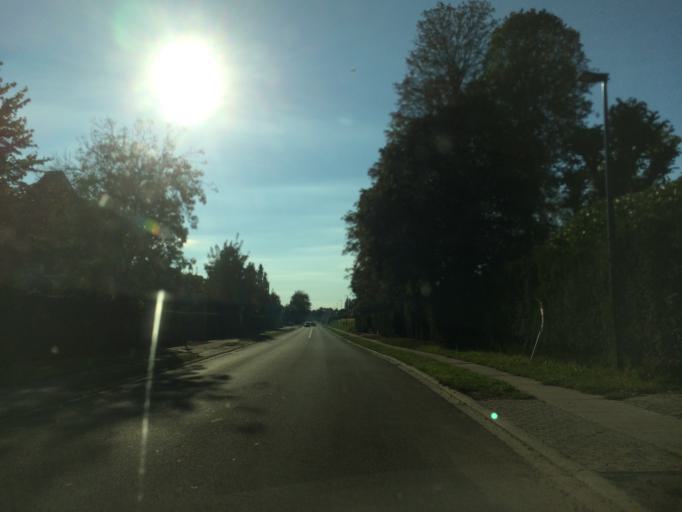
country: BE
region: Flanders
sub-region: Provincie Vlaams-Brabant
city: Bever
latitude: 50.9160
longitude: 4.3148
